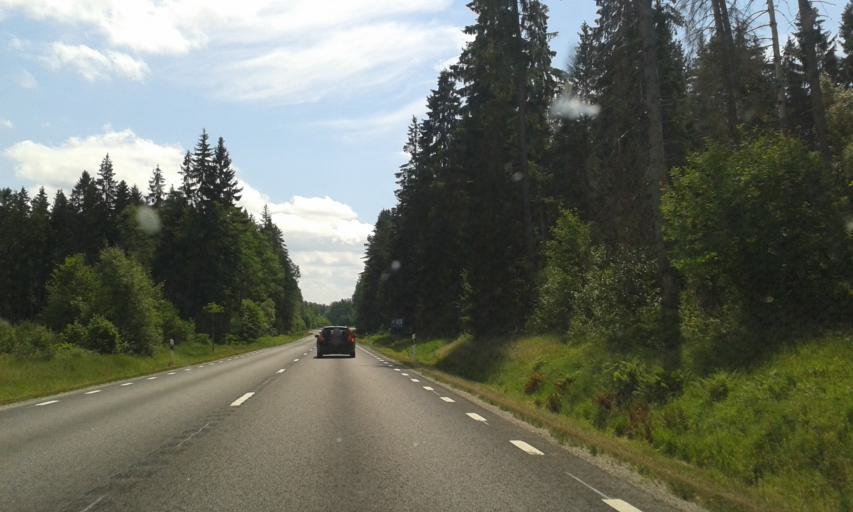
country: SE
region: Joenkoeping
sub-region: Varnamo Kommun
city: Rydaholm
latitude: 56.9915
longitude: 14.2949
